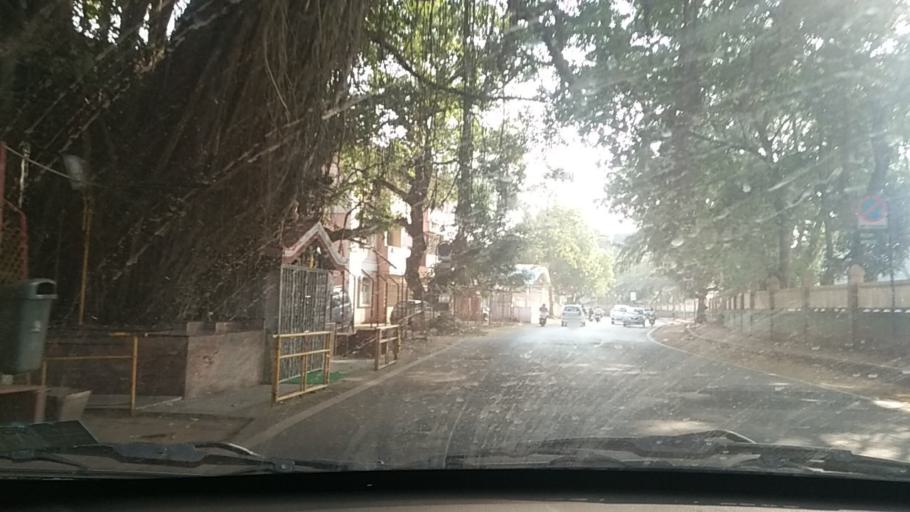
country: IN
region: Goa
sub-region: North Goa
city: Panaji
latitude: 15.4858
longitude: 73.8172
